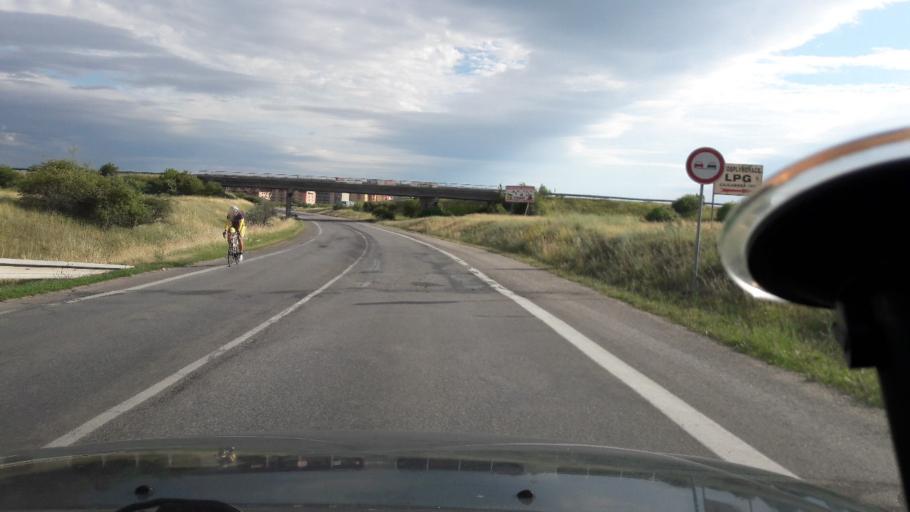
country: SK
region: Bratislavsky
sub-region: Okres Pezinok
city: Pezinok
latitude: 48.3024
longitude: 17.2822
